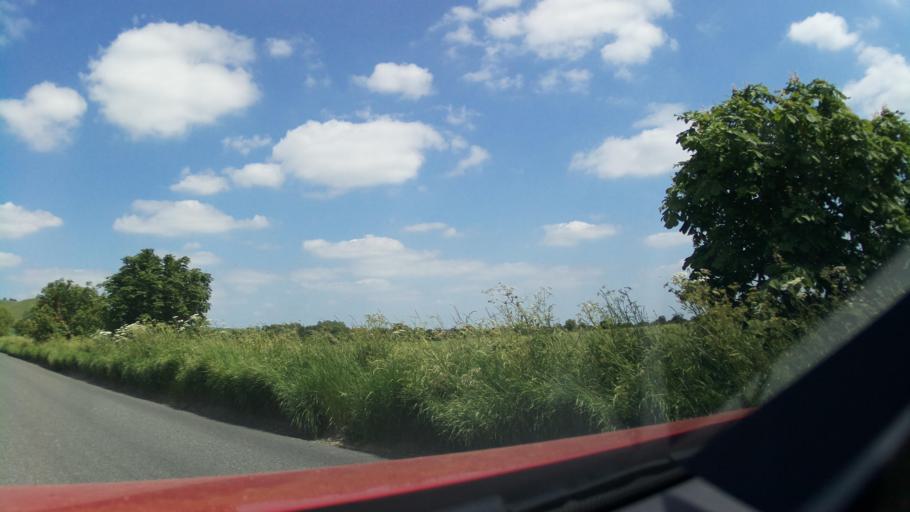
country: GB
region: England
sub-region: Wiltshire
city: Avebury
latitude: 51.3684
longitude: -1.8972
